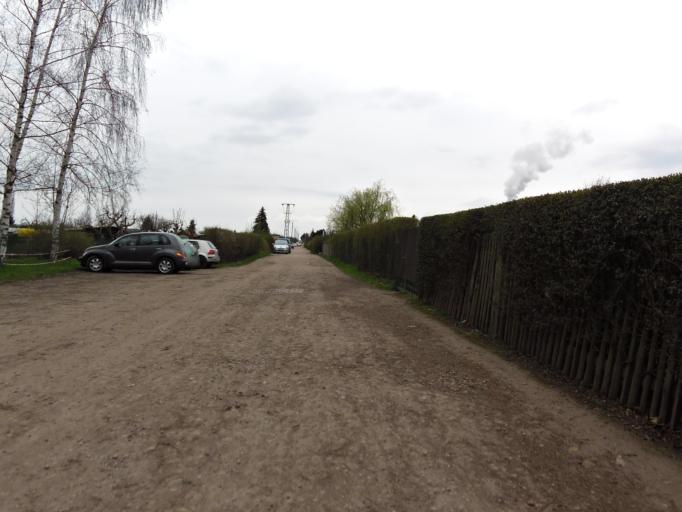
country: DE
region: Thuringia
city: Gotha
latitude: 50.9642
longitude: 10.7154
